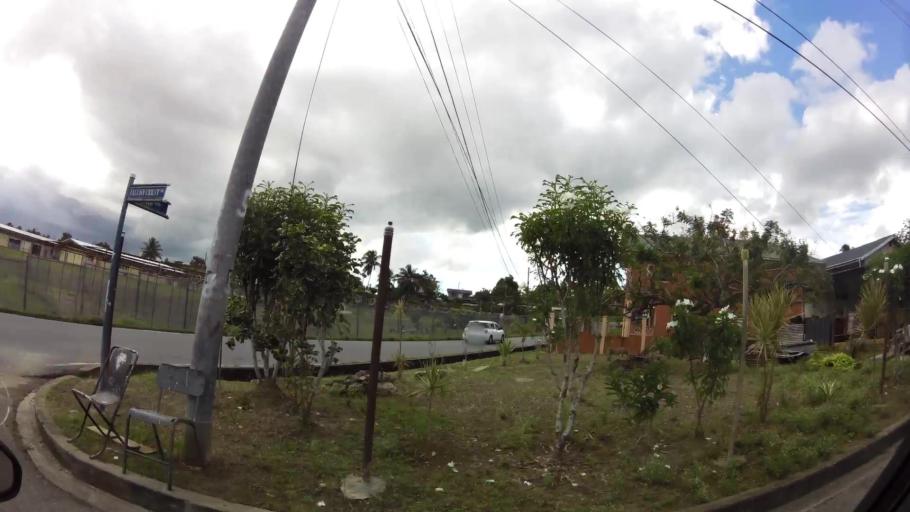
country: TT
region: City of San Fernando
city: Mon Repos
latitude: 10.2734
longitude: -61.4484
